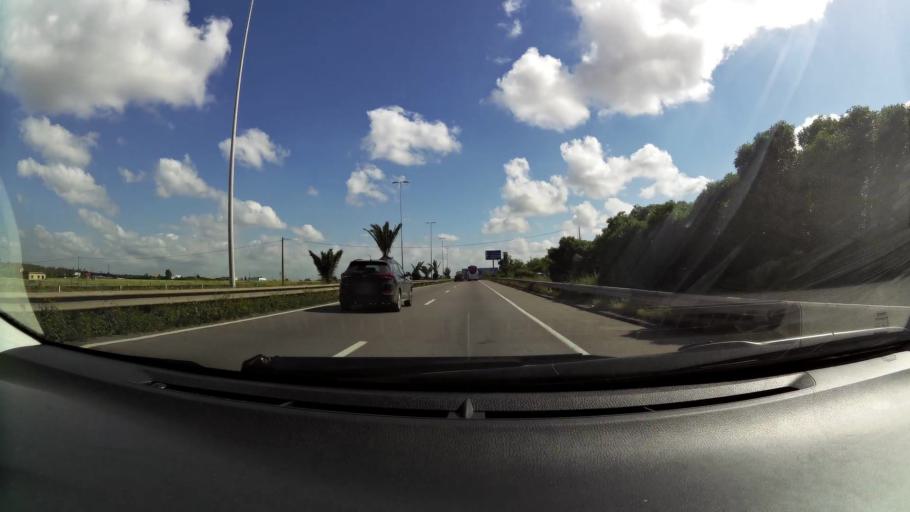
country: MA
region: Grand Casablanca
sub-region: Nouaceur
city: Bouskoura
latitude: 33.4512
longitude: -7.6334
